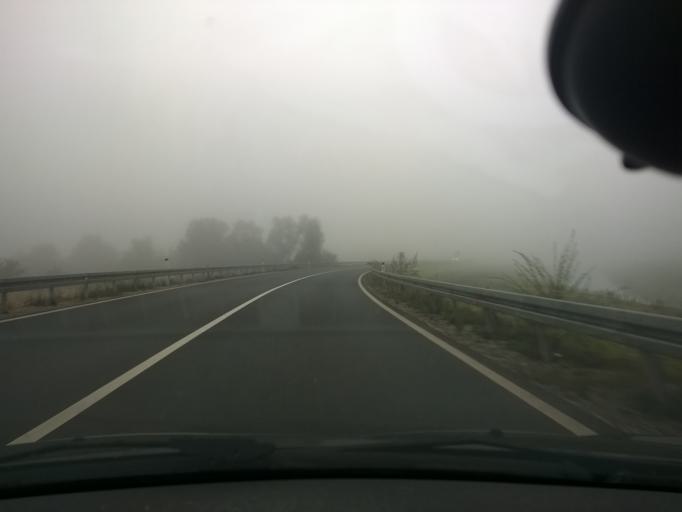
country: HR
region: Zagrebacka
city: Zapresic
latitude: 45.8812
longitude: 15.8198
